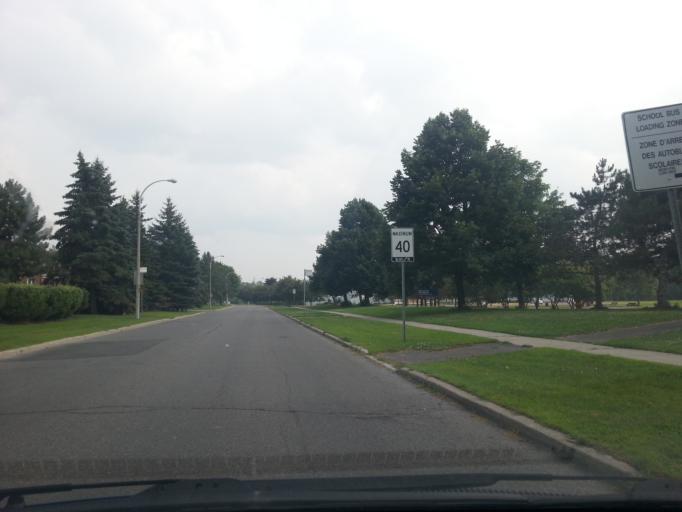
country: CA
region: Quebec
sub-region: Outaouais
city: Gatineau
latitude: 45.4796
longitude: -75.5307
